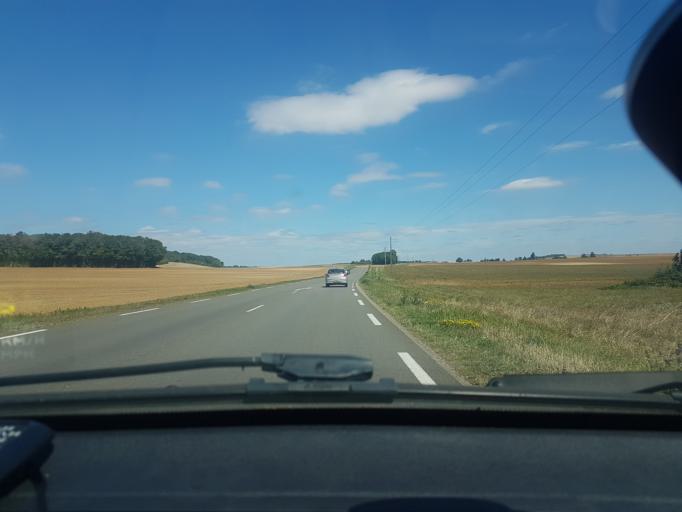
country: FR
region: Bourgogne
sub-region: Departement de la Cote-d'Or
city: Belleneuve
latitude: 47.3729
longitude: 5.2328
